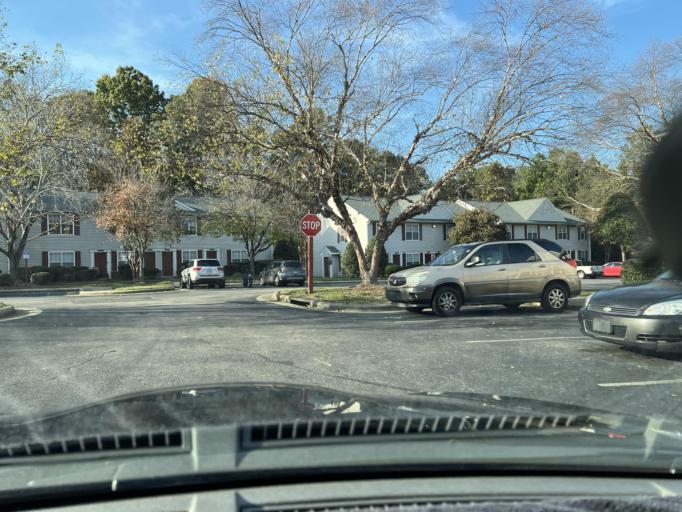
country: US
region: North Carolina
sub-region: Wake County
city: Raleigh
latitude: 35.8682
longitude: -78.5935
